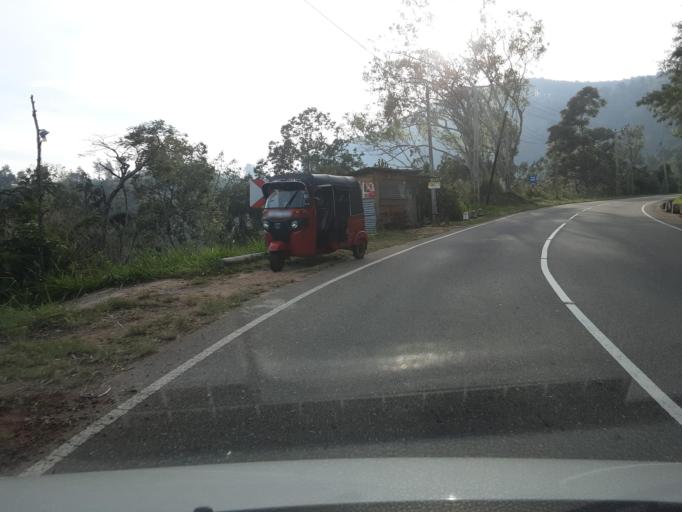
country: LK
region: Uva
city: Badulla
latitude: 6.9305
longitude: 80.9669
